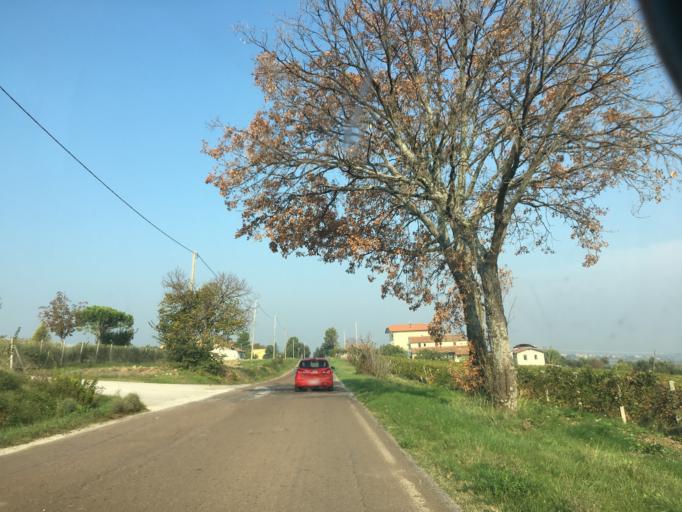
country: IT
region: Emilia-Romagna
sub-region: Provincia di Rimini
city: San Clemente
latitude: 43.9478
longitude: 12.6152
